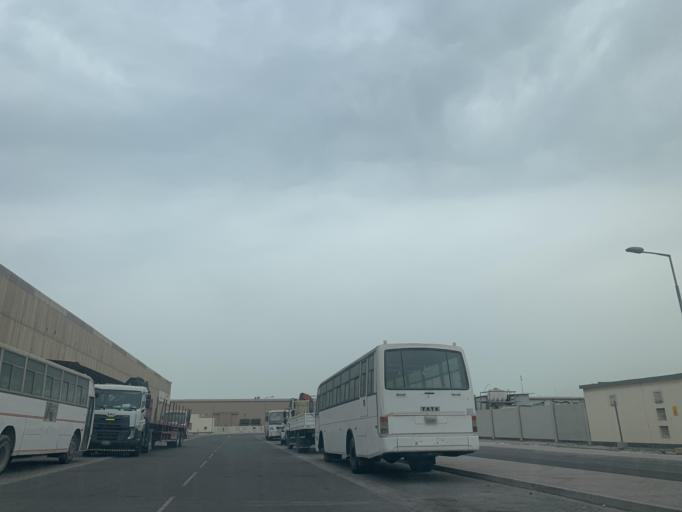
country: BH
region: Muharraq
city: Al Hadd
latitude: 26.2044
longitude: 50.6838
